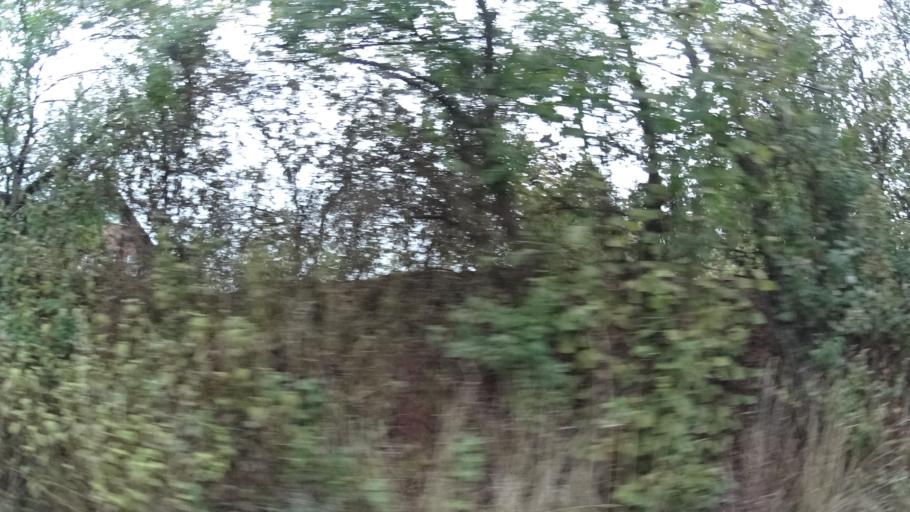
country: DE
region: Hesse
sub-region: Regierungsbezirk Kassel
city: Dipperz
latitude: 50.4855
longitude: 9.8043
